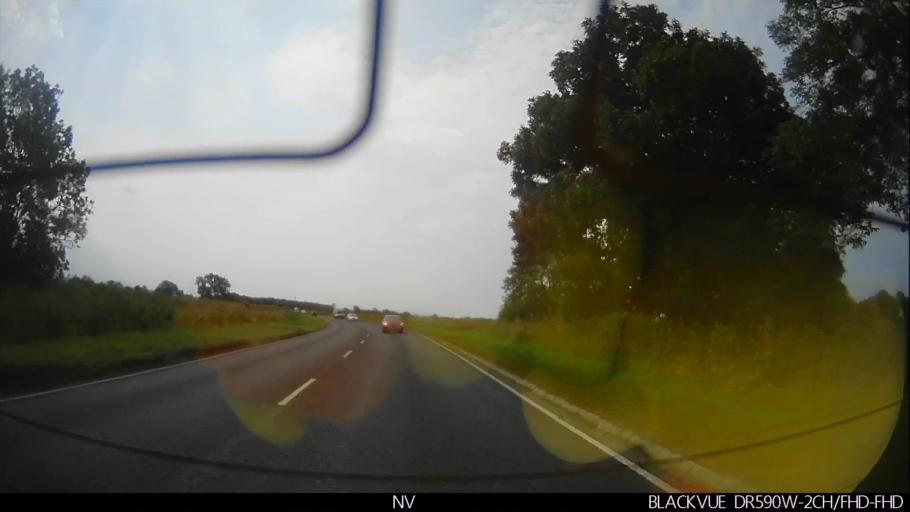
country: GB
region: England
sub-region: North Yorkshire
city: Marishes
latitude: 54.2042
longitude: -0.7718
